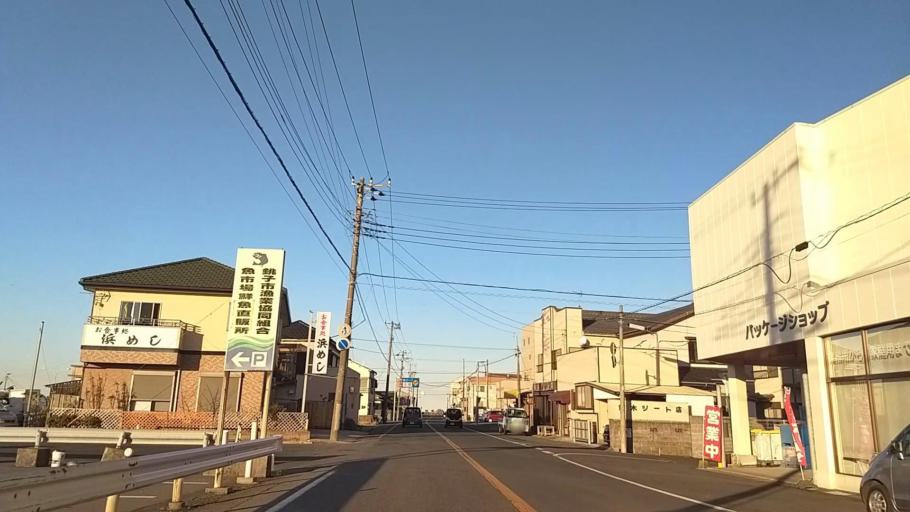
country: JP
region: Chiba
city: Hasaki
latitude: 35.7346
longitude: 140.8417
